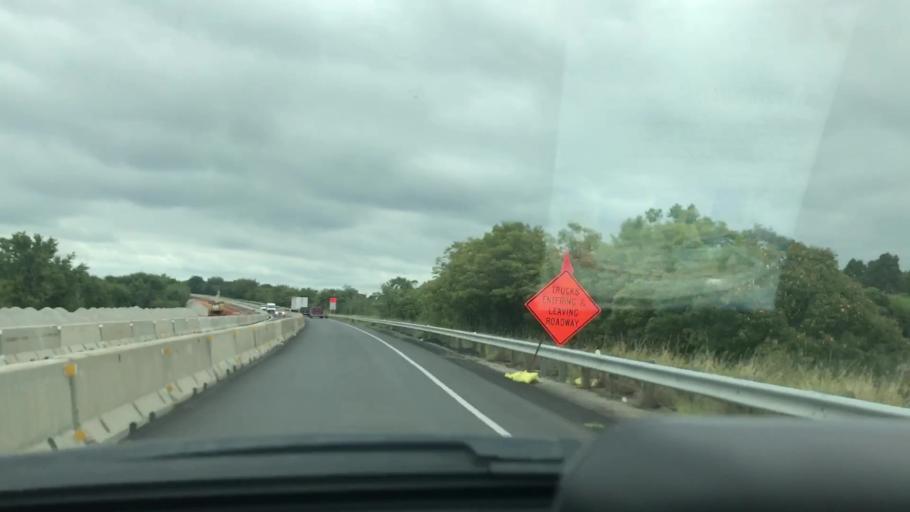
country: US
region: Oklahoma
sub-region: McIntosh County
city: Eufaula
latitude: 35.2474
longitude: -95.5850
